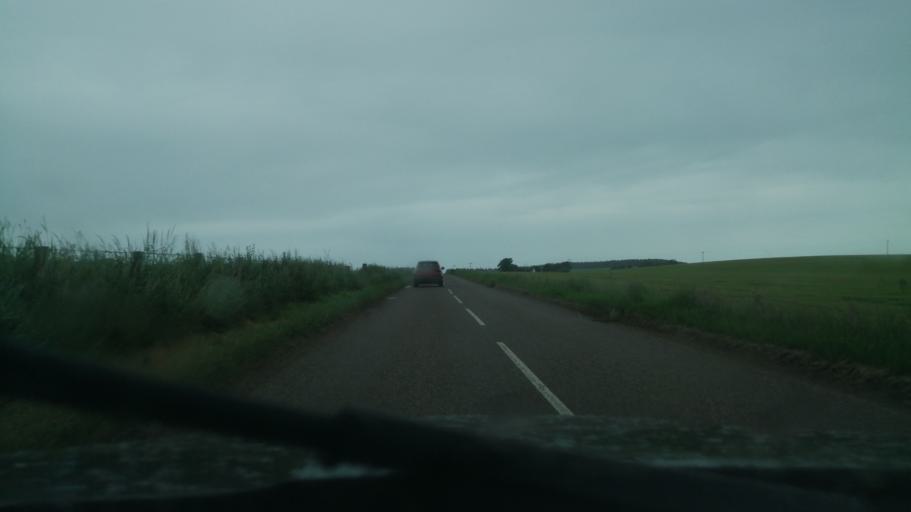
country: GB
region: Scotland
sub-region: Moray
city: Cullen
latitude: 57.6418
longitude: -2.8315
